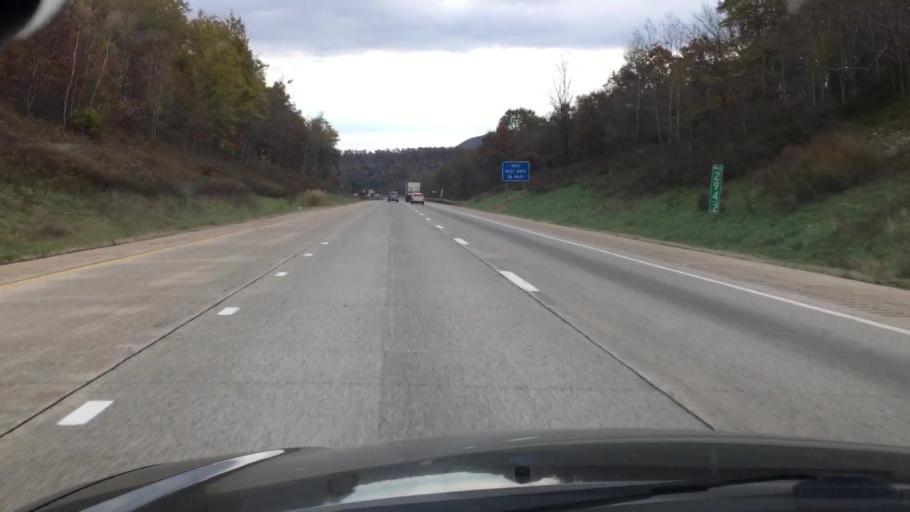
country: US
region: Pennsylvania
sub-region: Monroe County
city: Emerald Lakes
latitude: 41.0643
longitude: -75.3792
